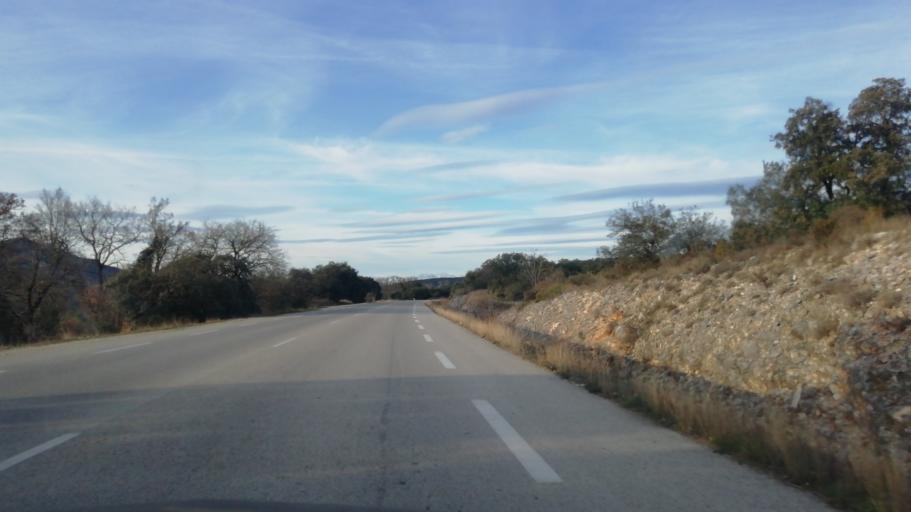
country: FR
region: Languedoc-Roussillon
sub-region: Departement du Gard
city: Quissac
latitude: 43.8963
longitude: 4.0082
